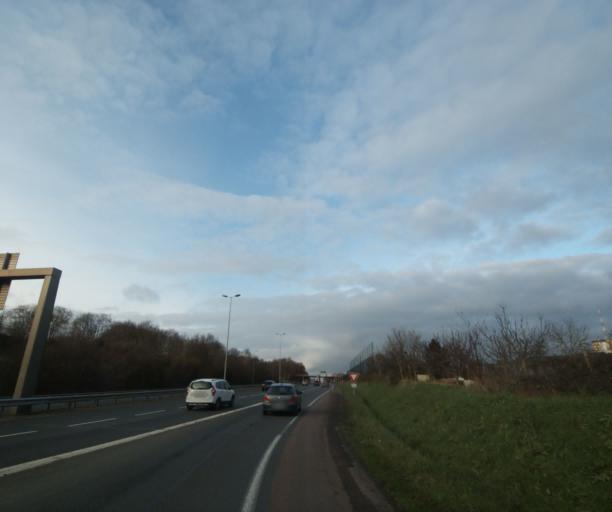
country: FR
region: Pays de la Loire
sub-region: Departement de la Sarthe
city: La Chapelle-Saint-Aubin
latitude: 48.0159
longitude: 0.1707
